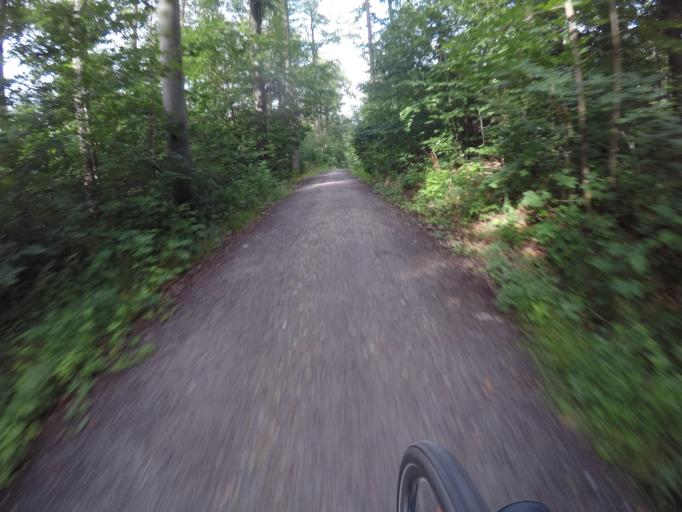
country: DE
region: Baden-Wuerttemberg
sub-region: Regierungsbezirk Stuttgart
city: Gerlingen
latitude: 48.7712
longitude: 9.1126
